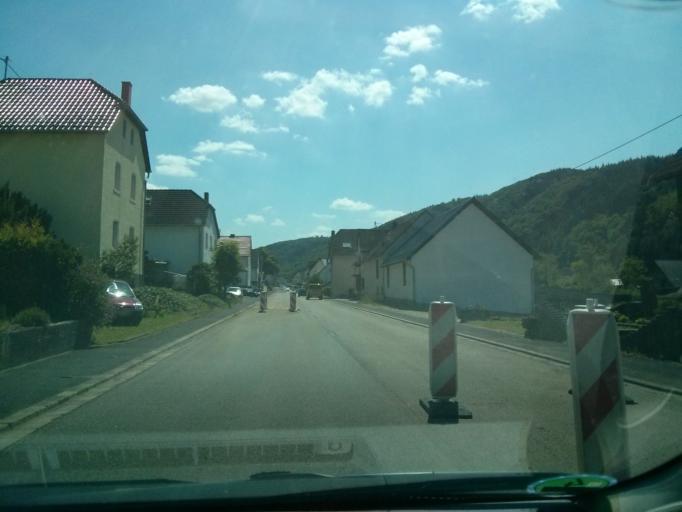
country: DE
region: Rheinland-Pfalz
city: Insul
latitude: 50.4317
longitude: 6.9333
